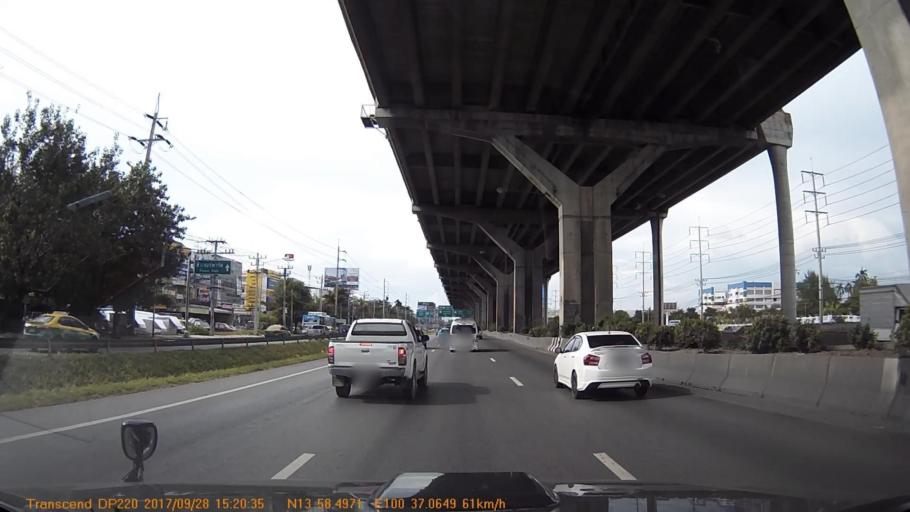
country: TH
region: Bangkok
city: Sai Mai
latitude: 13.9751
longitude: 100.6178
